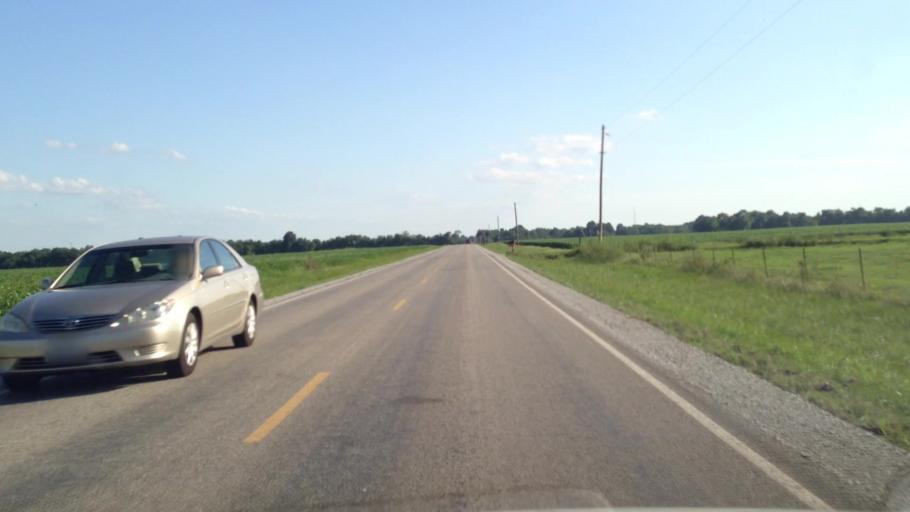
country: US
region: Kansas
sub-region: Crawford County
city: Pittsburg
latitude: 37.3600
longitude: -94.6315
